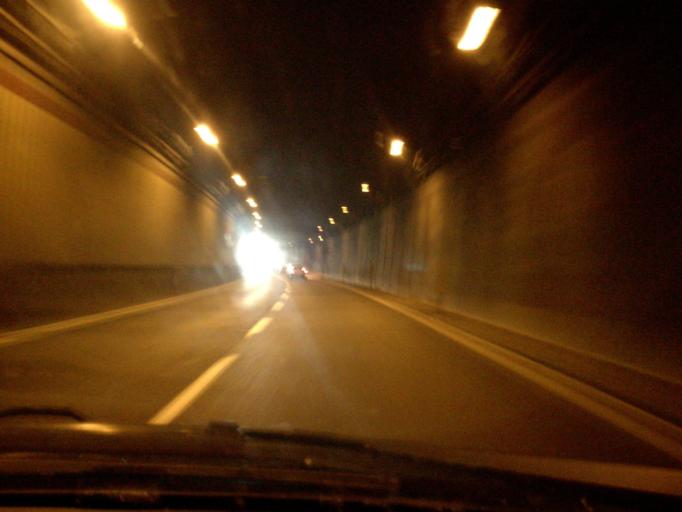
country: IT
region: Lombardy
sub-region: Provincia di Monza e Brianza
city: Monza
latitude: 45.5577
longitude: 9.2595
